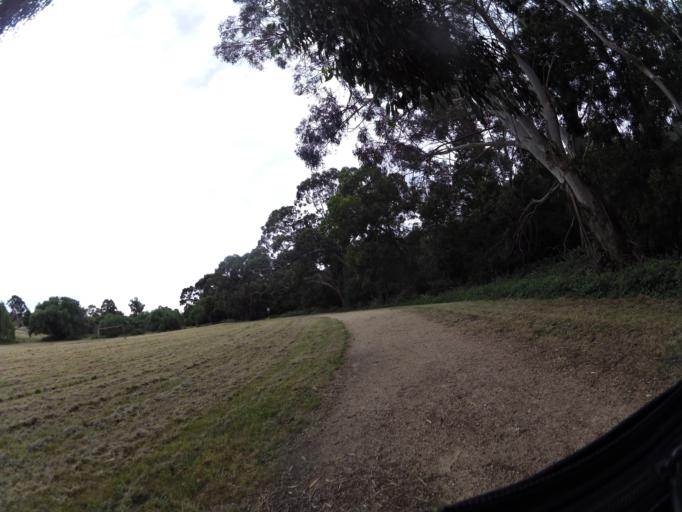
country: AU
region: Victoria
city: Brown Hill
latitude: -37.4305
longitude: 143.9011
